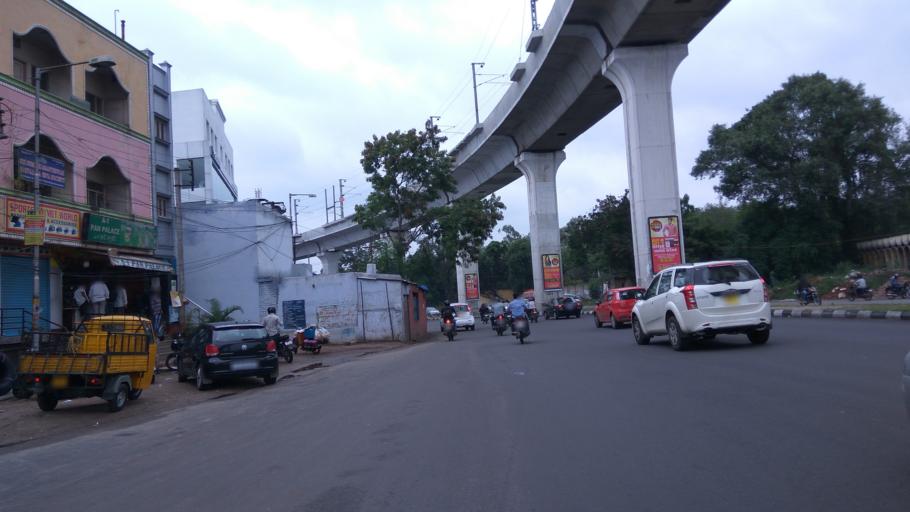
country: IN
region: Telangana
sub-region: Hyderabad
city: Malkajgiri
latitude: 17.4363
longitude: 78.5185
